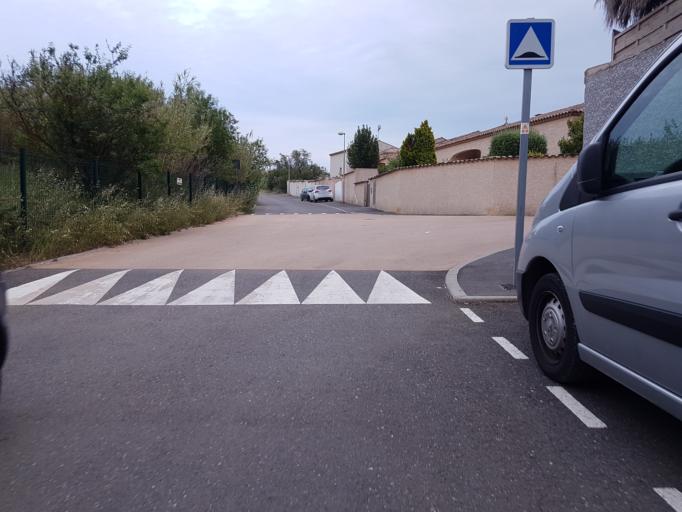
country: FR
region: Languedoc-Roussillon
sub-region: Departement de l'Herault
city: Cers
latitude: 43.3223
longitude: 3.3114
